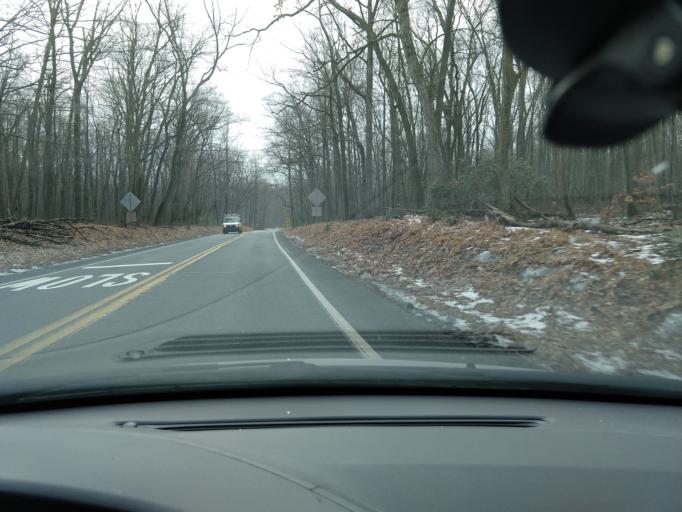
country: US
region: Pennsylvania
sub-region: Berks County
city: Birdsboro
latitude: 40.2164
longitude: -75.7761
